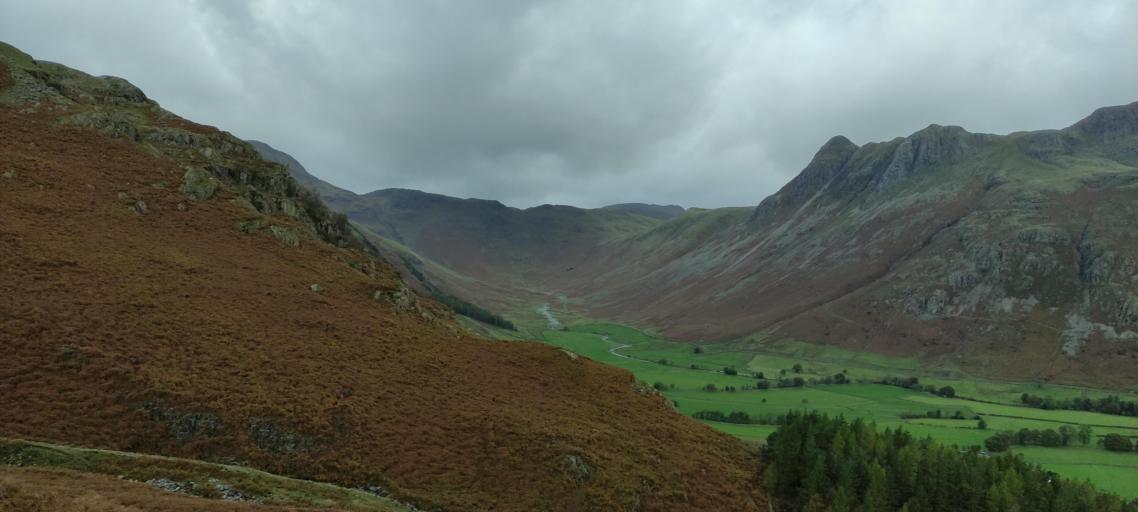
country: GB
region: England
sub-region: Cumbria
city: Ambleside
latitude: 54.4332
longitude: -3.1046
